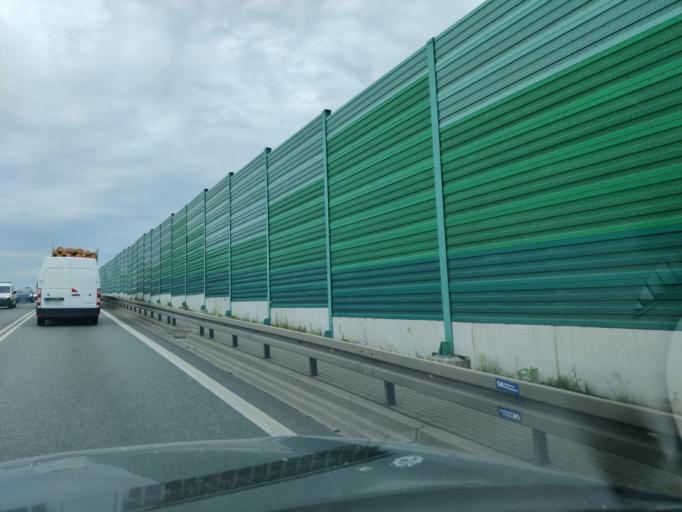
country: PL
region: Masovian Voivodeship
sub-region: Powiat minski
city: Minsk Mazowiecki
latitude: 52.2073
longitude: 21.5368
